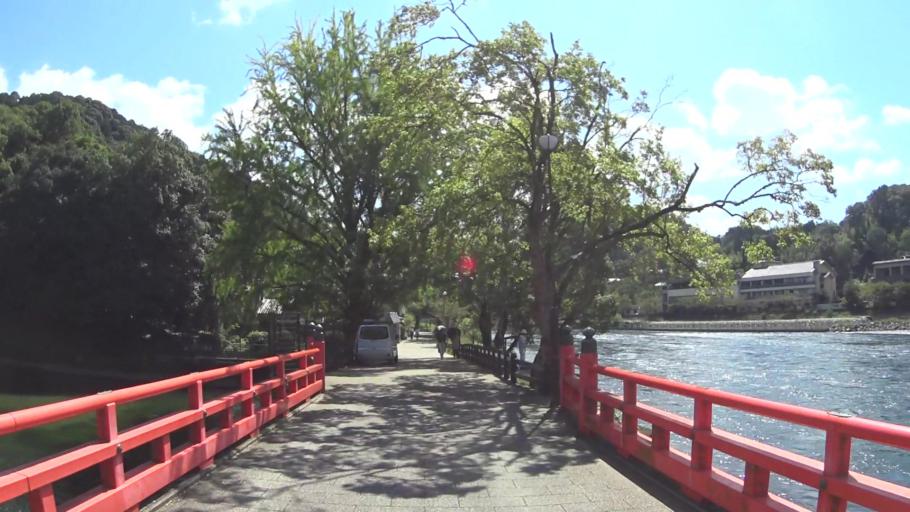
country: JP
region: Kyoto
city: Uji
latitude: 34.8891
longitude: 135.8112
